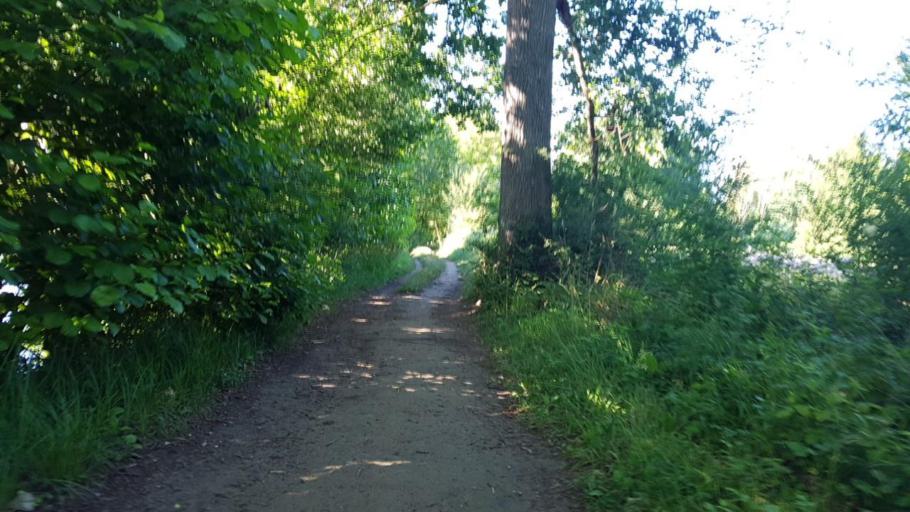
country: FR
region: Picardie
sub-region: Departement de l'Aisne
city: Essomes-sur-Marne
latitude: 49.0192
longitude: 3.3792
